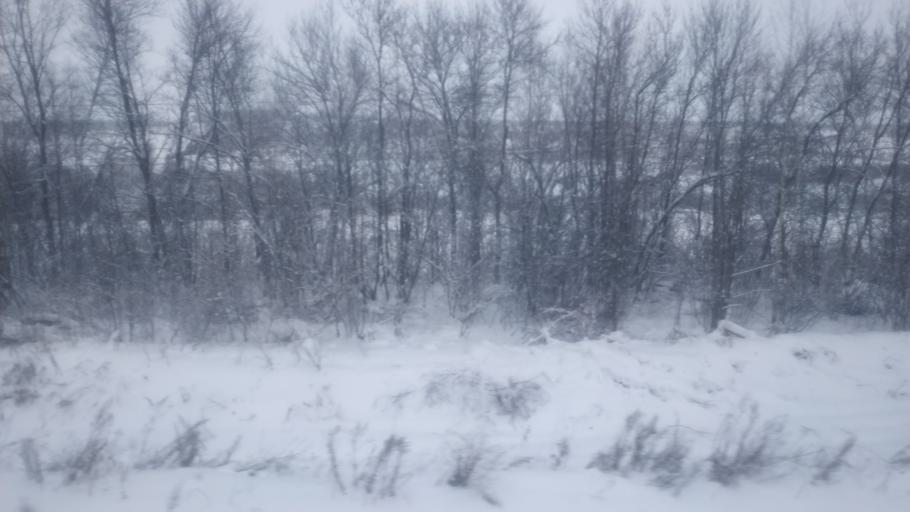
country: RU
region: Udmurtiya
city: Kiyasovo
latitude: 56.5015
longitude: 53.3772
